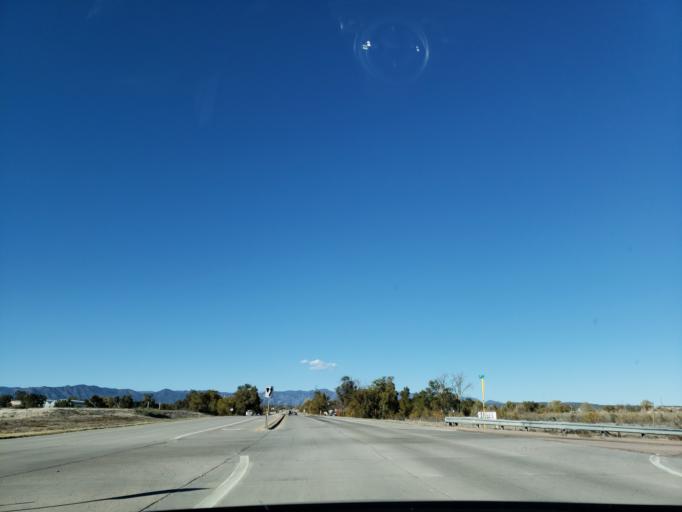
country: US
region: Colorado
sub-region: Fremont County
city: Penrose
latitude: 38.4320
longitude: -105.0240
